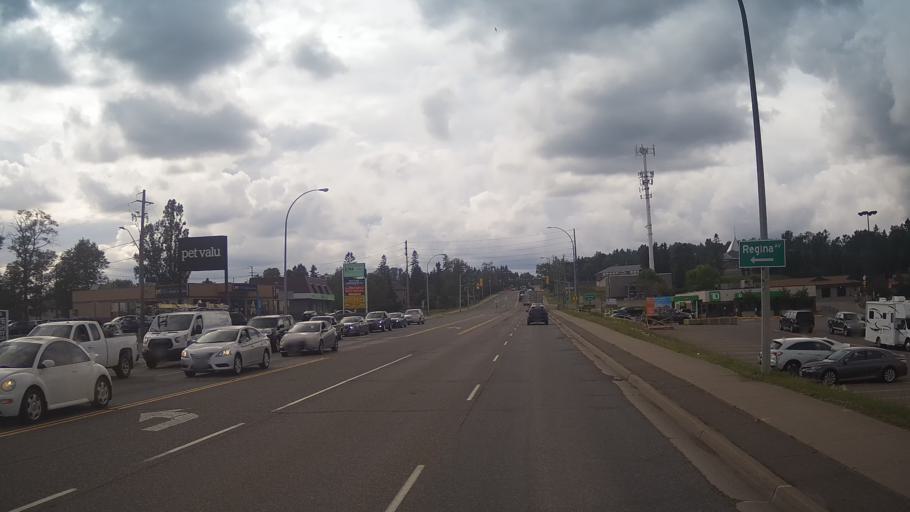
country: CA
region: Ontario
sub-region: Thunder Bay District
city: Thunder Bay
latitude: 48.4519
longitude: -89.2545
